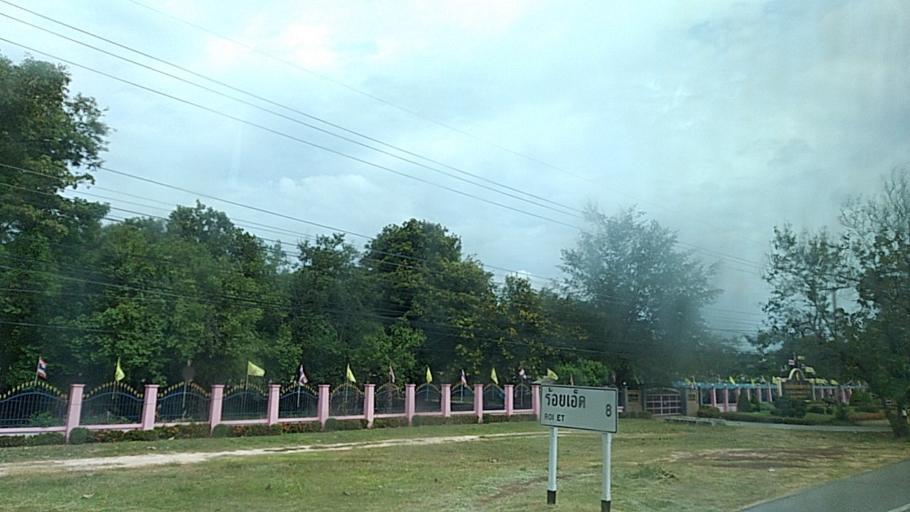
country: TH
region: Roi Et
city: Changhan
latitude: 16.0764
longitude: 103.5870
